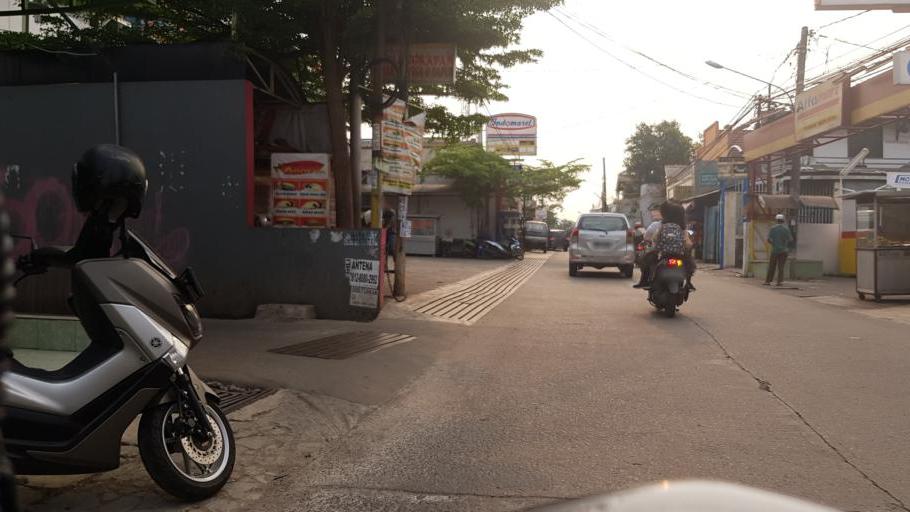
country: ID
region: West Java
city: Depok
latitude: -6.3723
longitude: 106.8518
